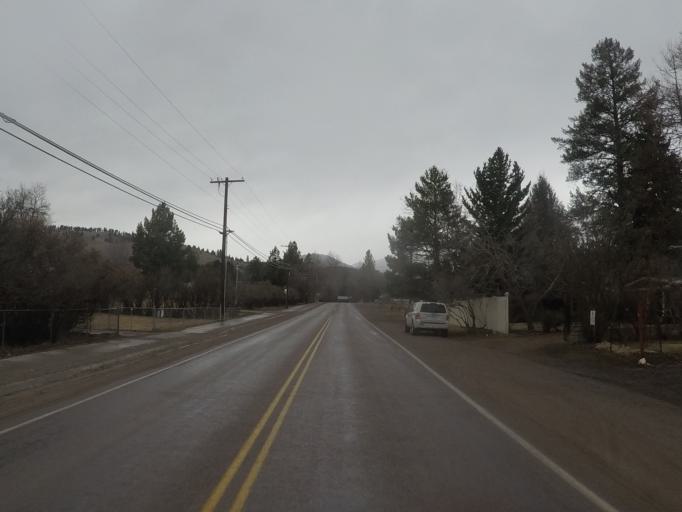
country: US
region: Montana
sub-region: Missoula County
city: East Missoula
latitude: 46.8979
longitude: -113.9656
